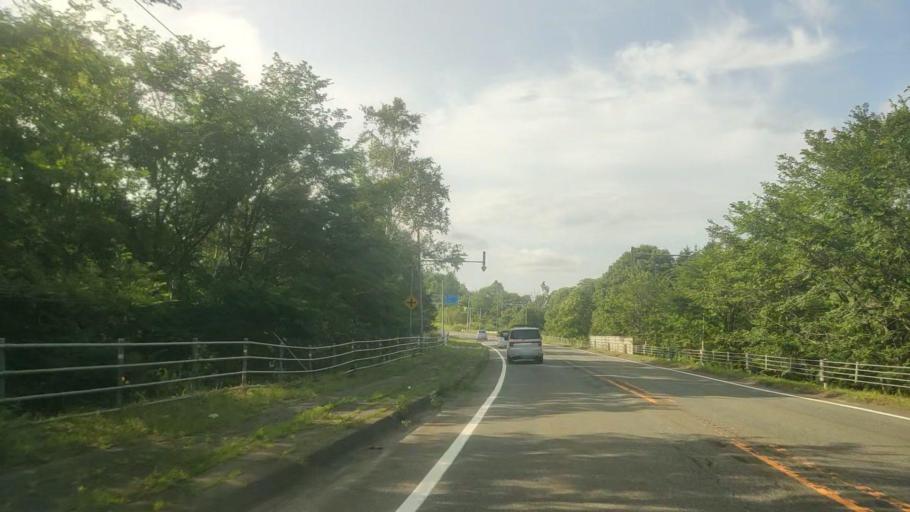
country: JP
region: Hokkaido
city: Chitose
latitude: 42.8734
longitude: 141.8221
